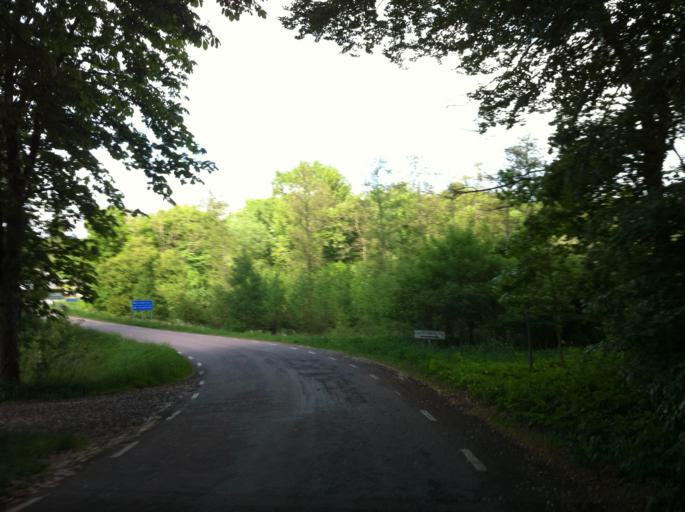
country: SE
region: Skane
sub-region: Svalovs Kommun
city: Kagerod
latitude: 56.0365
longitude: 13.1593
